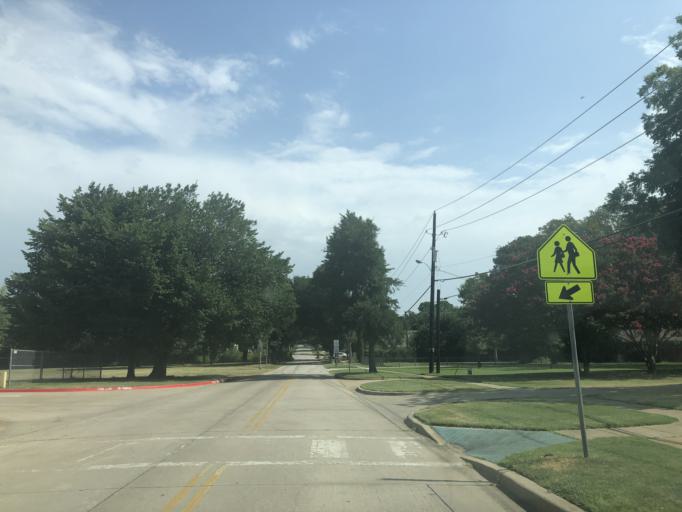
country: US
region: Texas
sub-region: Dallas County
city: Grand Prairie
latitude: 32.7718
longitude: -97.0430
